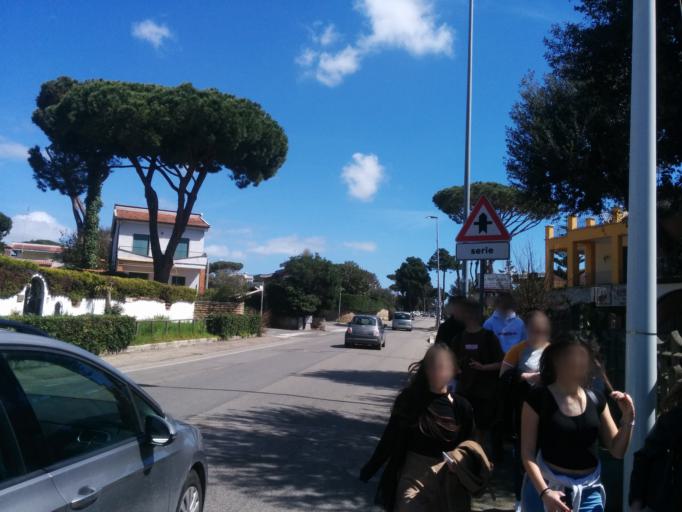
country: IT
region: Latium
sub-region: Citta metropolitana di Roma Capitale
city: Lavinio
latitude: 41.5021
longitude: 12.5940
